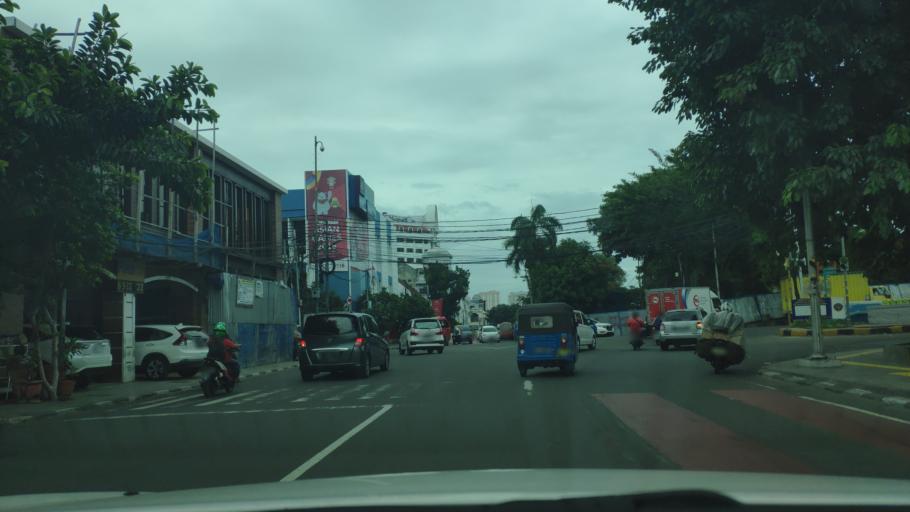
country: ID
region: Jakarta Raya
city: Jakarta
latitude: -6.1345
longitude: 106.8111
